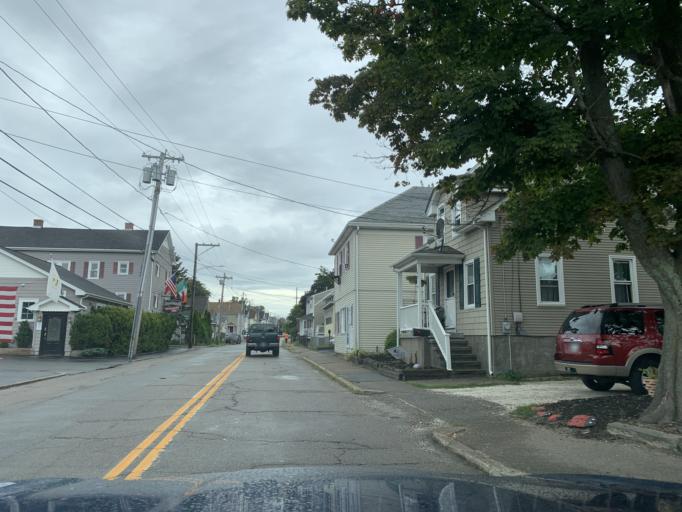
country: US
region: Rhode Island
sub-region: Bristol County
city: Warren
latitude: 41.7309
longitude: -71.2772
